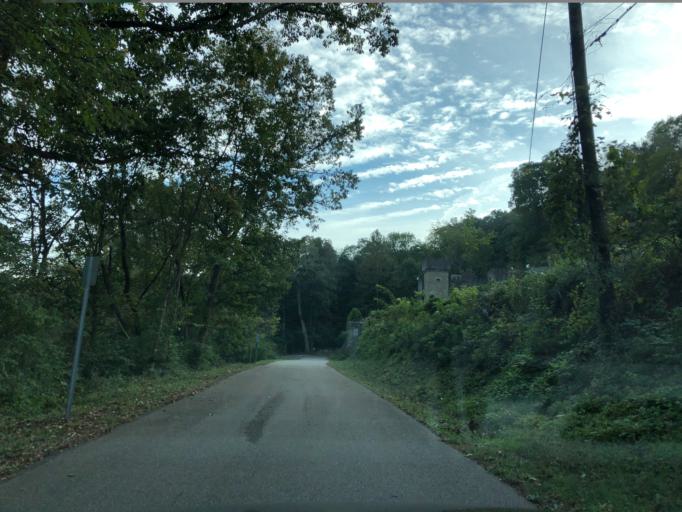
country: US
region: Ohio
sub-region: Hamilton County
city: Loveland
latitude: 39.2844
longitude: -84.2654
